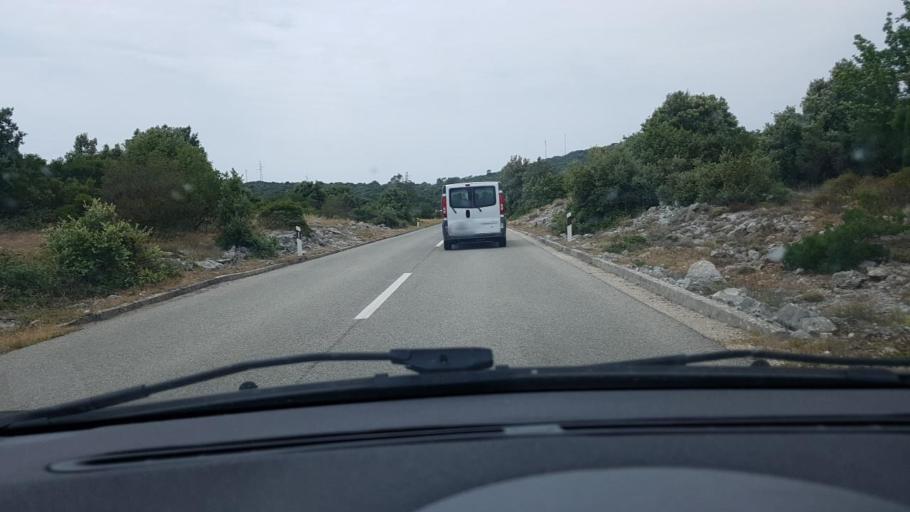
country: HR
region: Dubrovacko-Neretvanska
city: Smokvica
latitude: 42.9483
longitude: 16.9921
